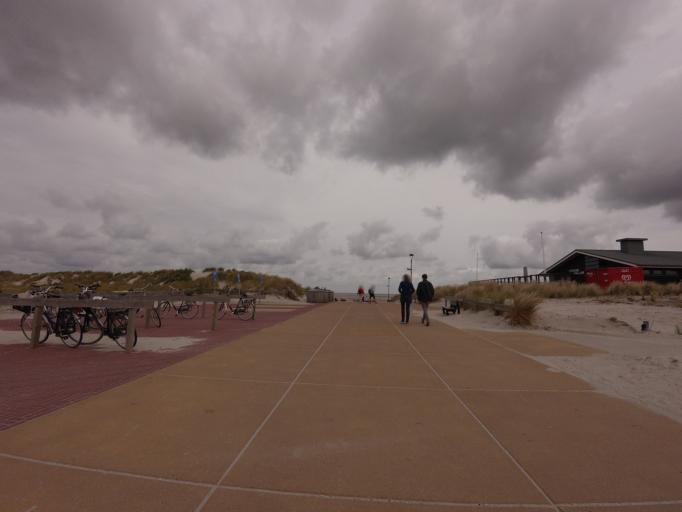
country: NL
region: Friesland
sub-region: Gemeente Ameland
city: Hollum
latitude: 53.4591
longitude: 5.6856
